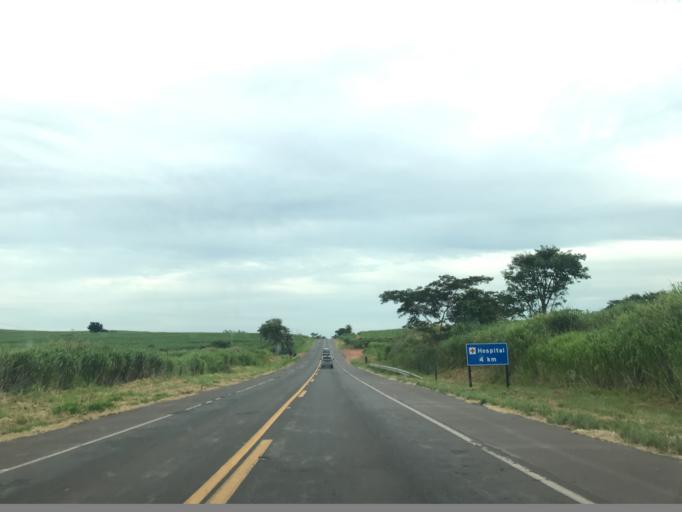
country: BR
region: Sao Paulo
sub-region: Tupa
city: Tupa
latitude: -21.6017
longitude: -50.4687
